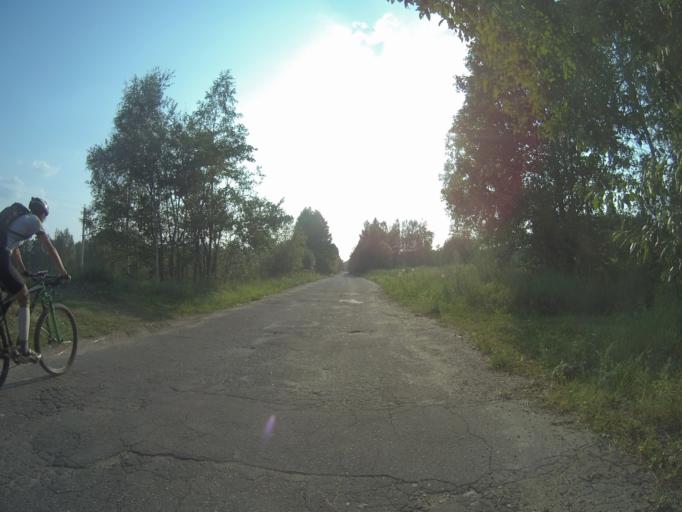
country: RU
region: Vladimir
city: Orgtrud
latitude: 56.2837
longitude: 40.7409
